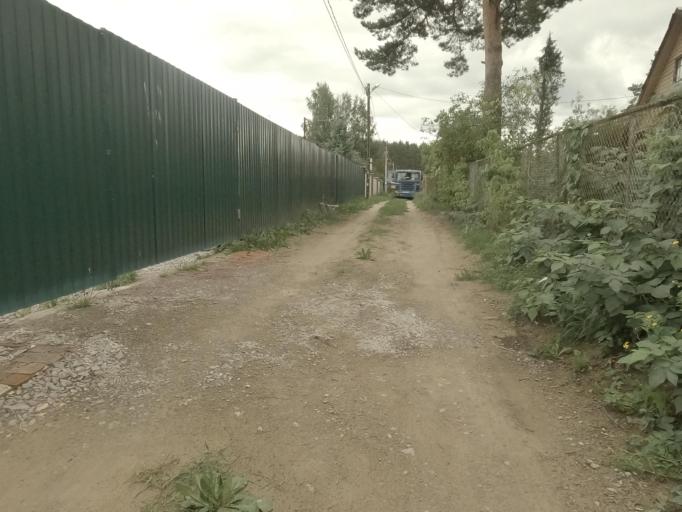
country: RU
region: Leningrad
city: Kirovsk
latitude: 59.8967
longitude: 31.0069
